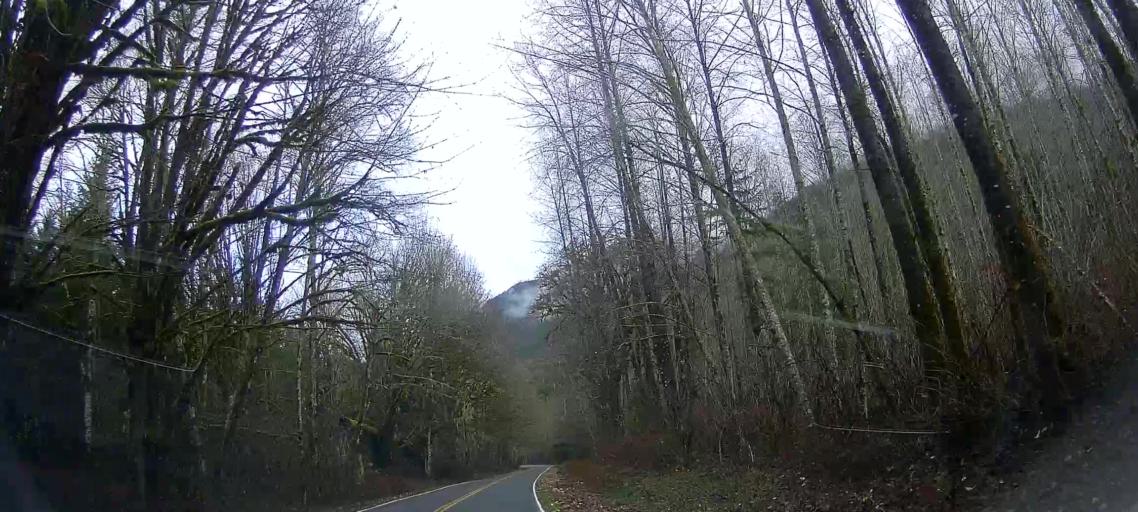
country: US
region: Washington
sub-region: Snohomish County
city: Darrington
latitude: 48.4958
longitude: -121.4695
